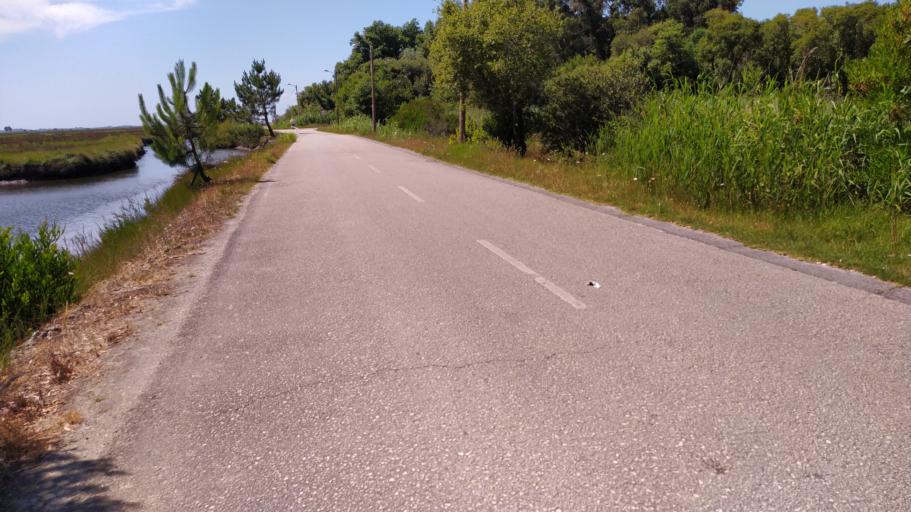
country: PT
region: Aveiro
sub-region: Aveiro
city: Aveiro
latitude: 40.6557
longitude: -8.6336
